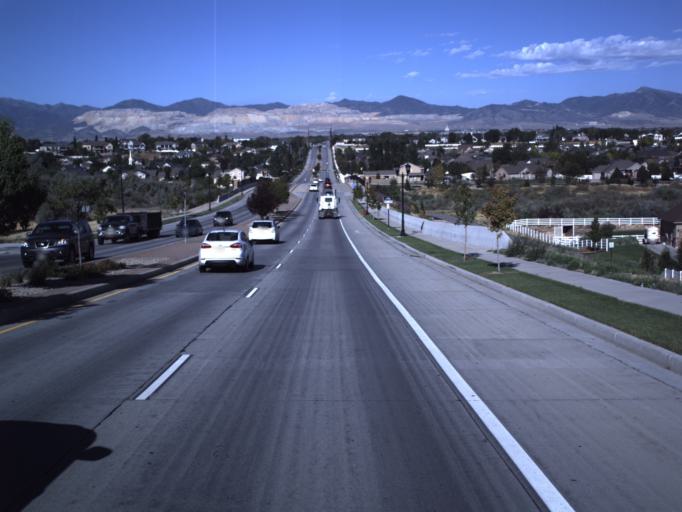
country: US
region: Utah
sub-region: Salt Lake County
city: South Jordan
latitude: 40.5444
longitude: -111.9132
